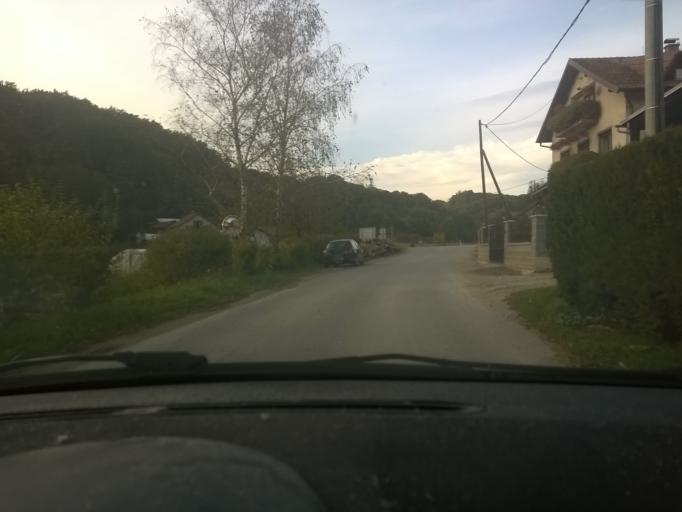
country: HR
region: Krapinsko-Zagorska
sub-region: Grad Krapina
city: Krapina
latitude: 46.1031
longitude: 15.8683
